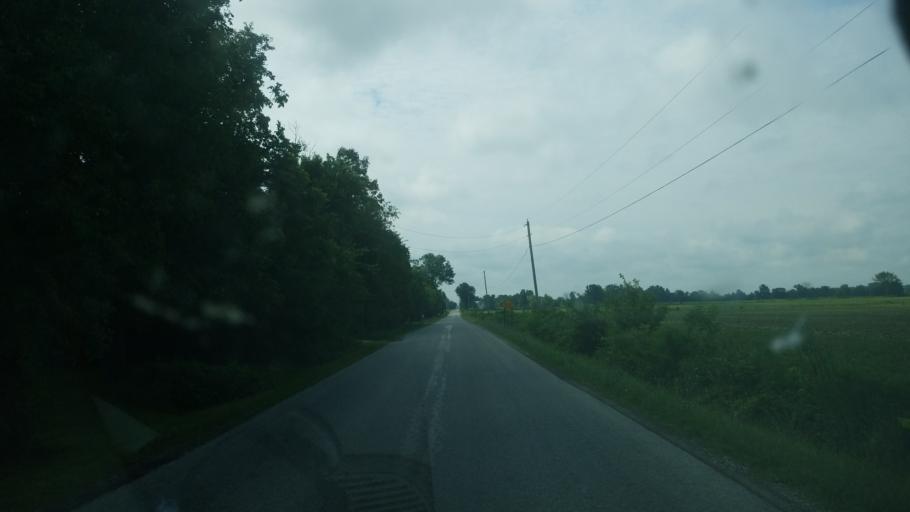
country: US
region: Ohio
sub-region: Licking County
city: Johnstown
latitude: 40.1869
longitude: -82.7574
